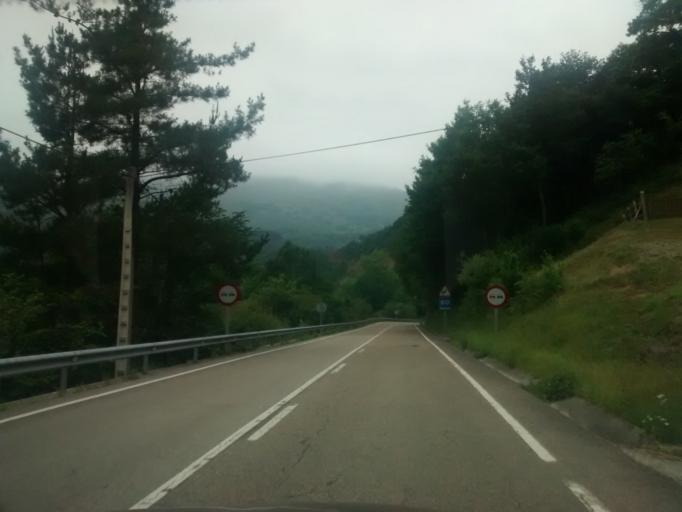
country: ES
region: Cantabria
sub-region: Provincia de Cantabria
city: Ruente
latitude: 43.1675
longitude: -4.2756
